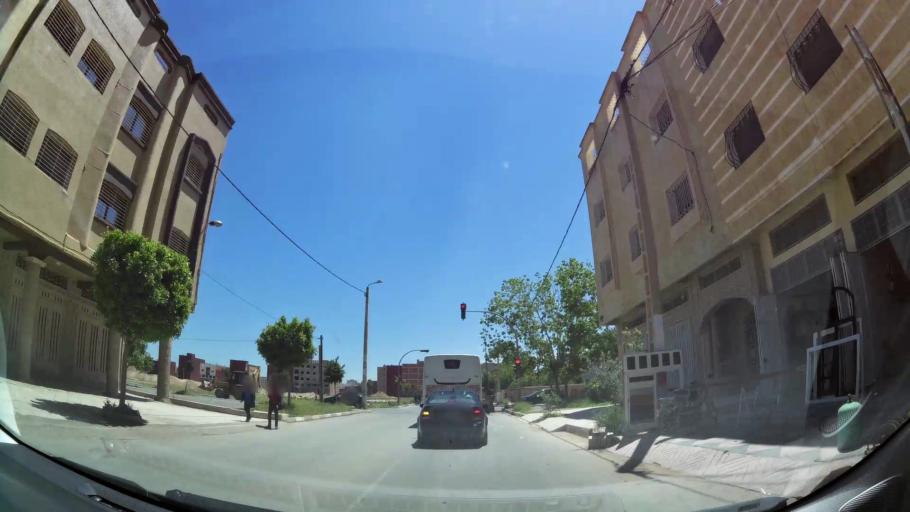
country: MA
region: Oriental
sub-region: Oujda-Angad
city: Oujda
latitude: 34.6706
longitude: -1.8825
